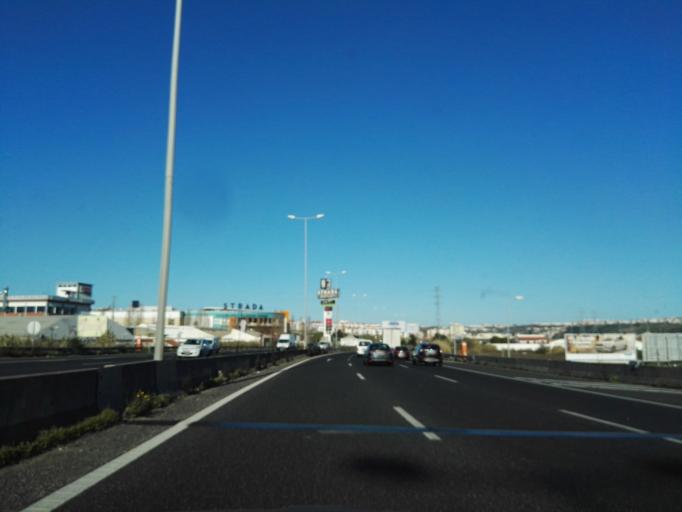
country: PT
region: Lisbon
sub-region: Odivelas
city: Pontinha
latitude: 38.7785
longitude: -9.1945
